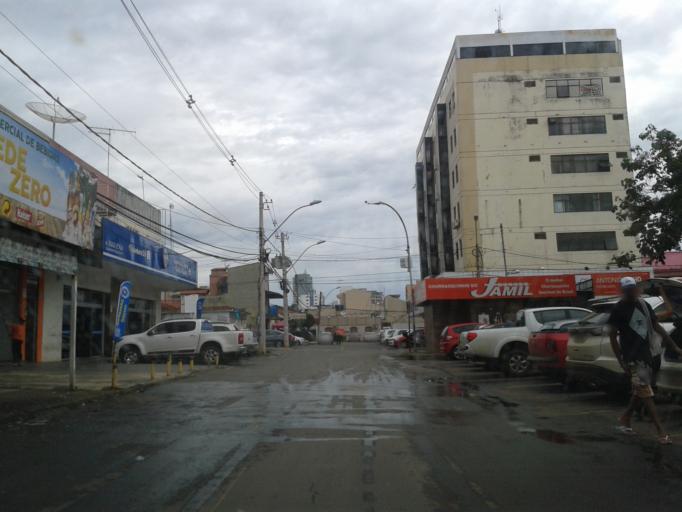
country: BR
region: Federal District
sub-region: Brasilia
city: Brasilia
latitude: -15.8270
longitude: -48.0568
